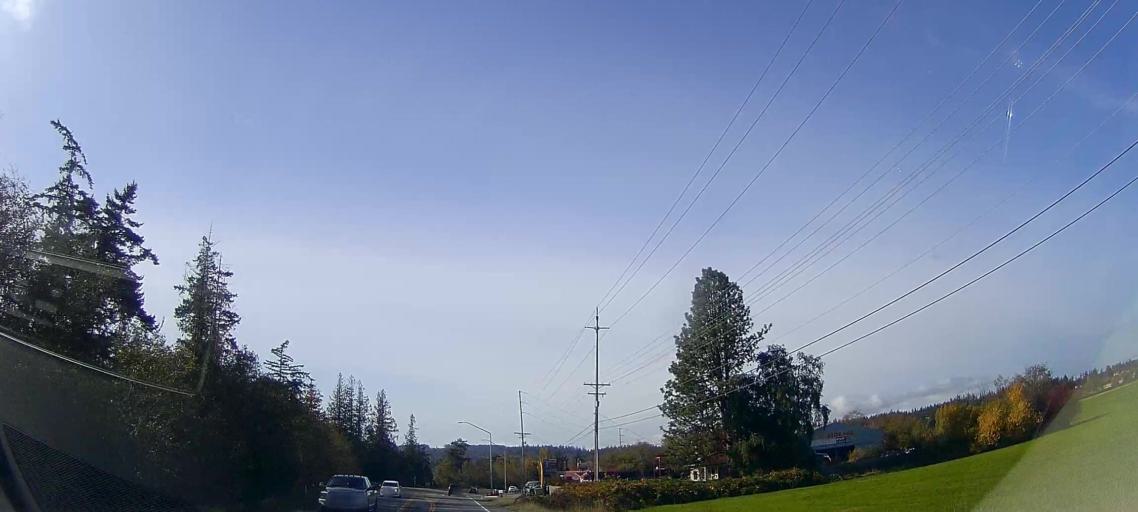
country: US
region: Washington
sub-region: Snohomish County
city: Stanwood
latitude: 48.2400
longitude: -122.4320
